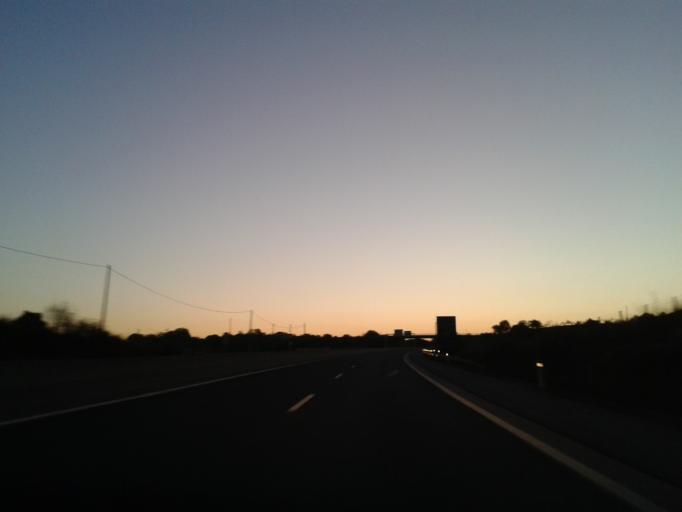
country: PT
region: Faro
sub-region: Albufeira
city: Guia
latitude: 37.1392
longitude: -8.3120
